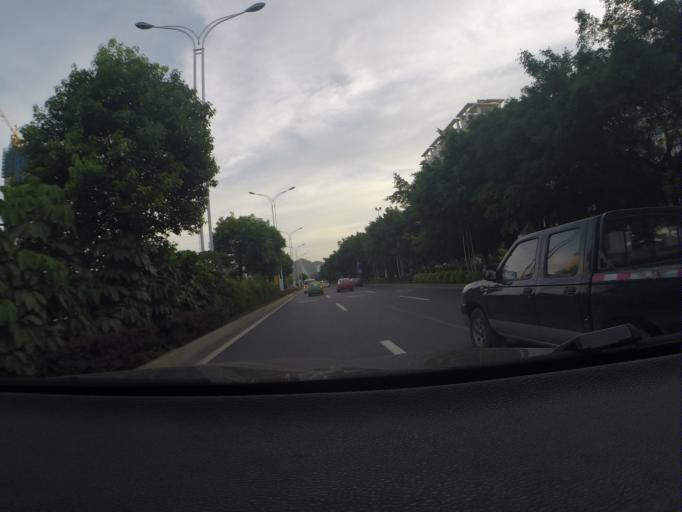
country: CN
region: Guangdong
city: Tangjiawan
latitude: 22.3574
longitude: 113.5919
